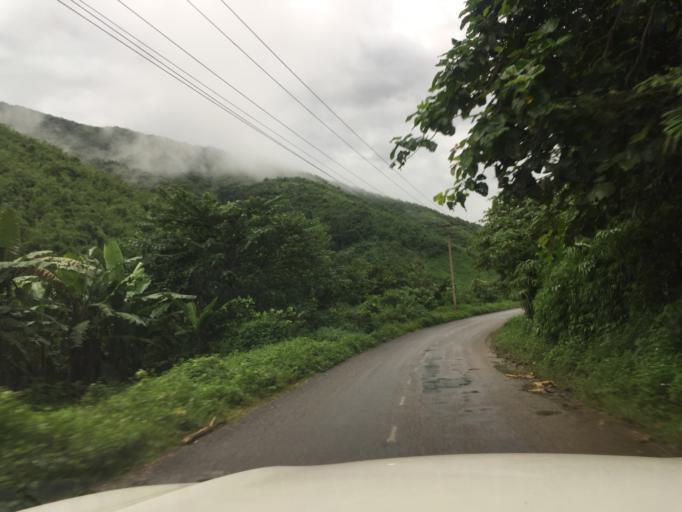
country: LA
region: Oudomxai
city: Muang La
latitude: 21.0428
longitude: 102.2416
